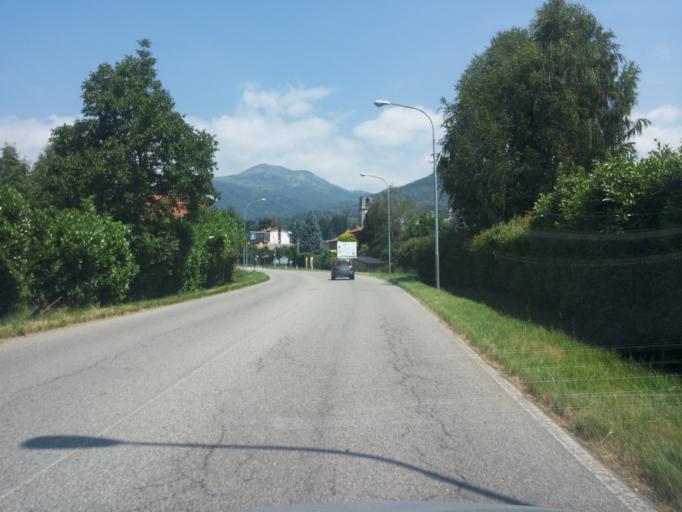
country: IT
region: Piedmont
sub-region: Provincia di Biella
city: Andorno Cacciorna
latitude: 45.6083
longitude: 8.0534
